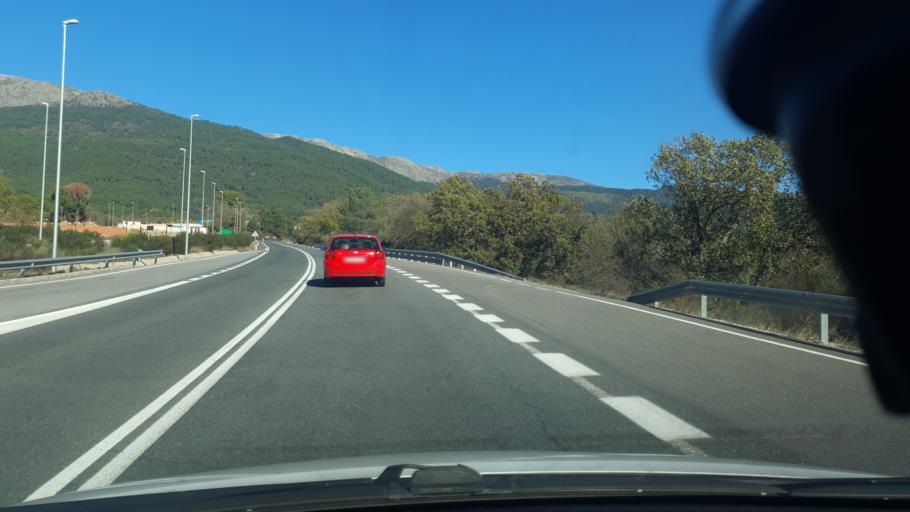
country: ES
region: Castille and Leon
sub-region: Provincia de Avila
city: Piedralaves
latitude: 40.2945
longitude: -4.7215
